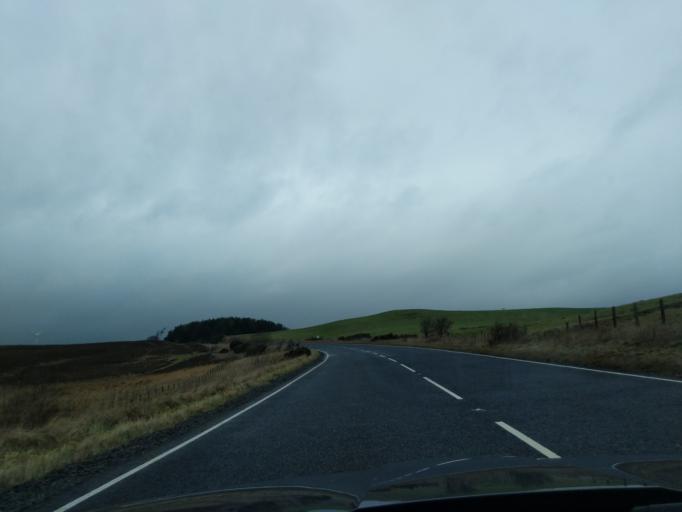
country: GB
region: England
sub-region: Northumberland
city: Rothley
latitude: 55.1736
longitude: -2.0263
